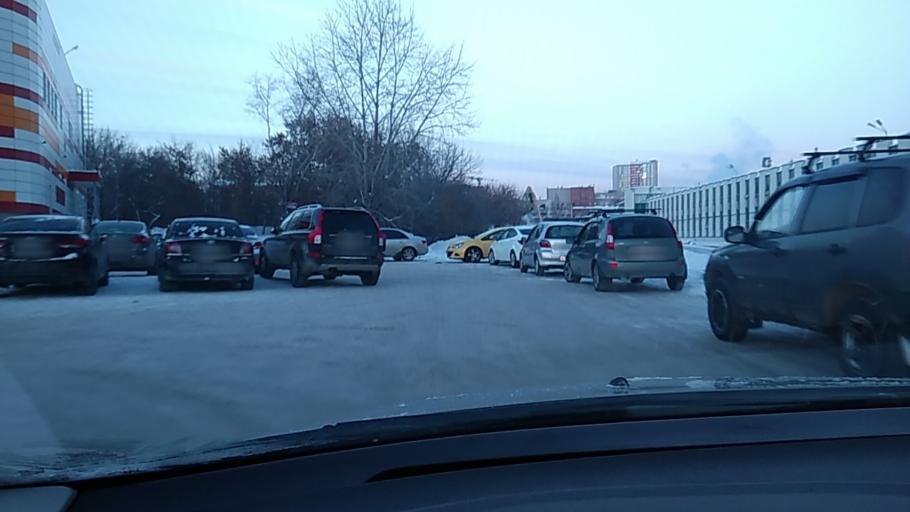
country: RU
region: Sverdlovsk
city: Yekaterinburg
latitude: 56.8217
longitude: 60.6411
